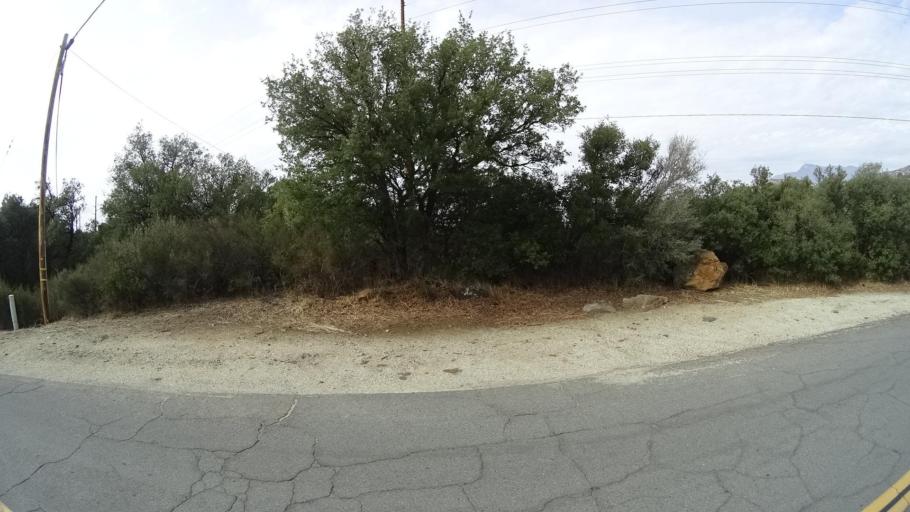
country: US
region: California
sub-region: San Diego County
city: Descanso
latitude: 32.8657
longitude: -116.6304
